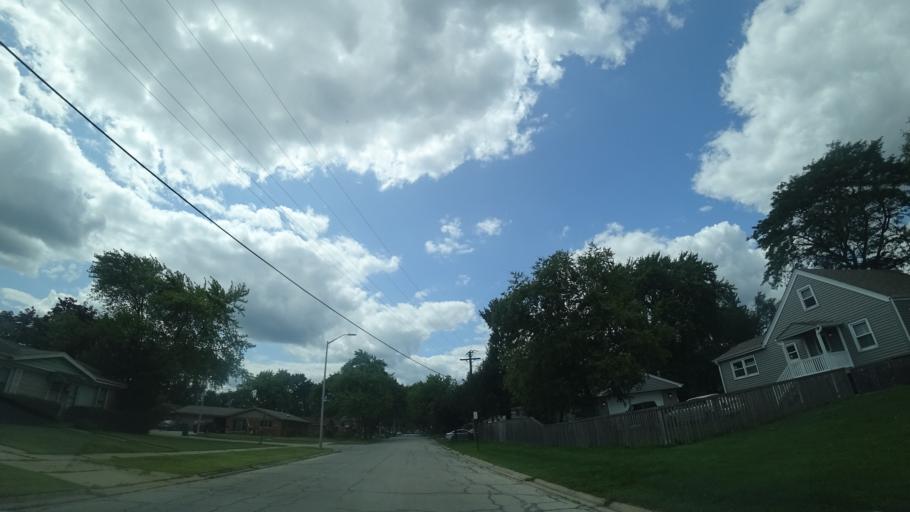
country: US
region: Illinois
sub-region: Cook County
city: Alsip
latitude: 41.6803
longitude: -87.7236
